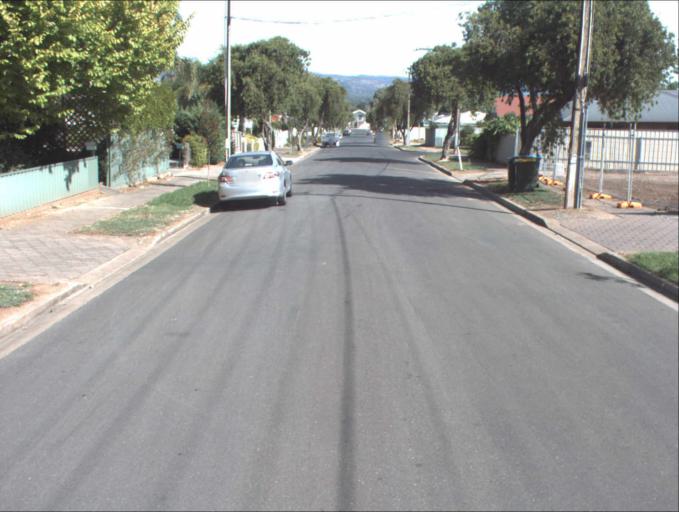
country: AU
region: South Australia
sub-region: Port Adelaide Enfield
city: Klemzig
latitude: -34.8744
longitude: 138.6397
